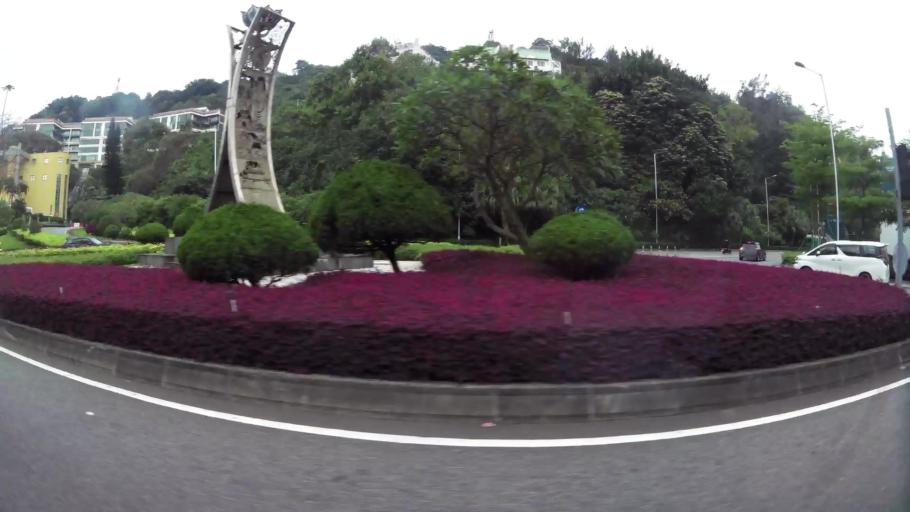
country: MO
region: Macau
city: Macau
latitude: 22.1965
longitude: 113.5529
